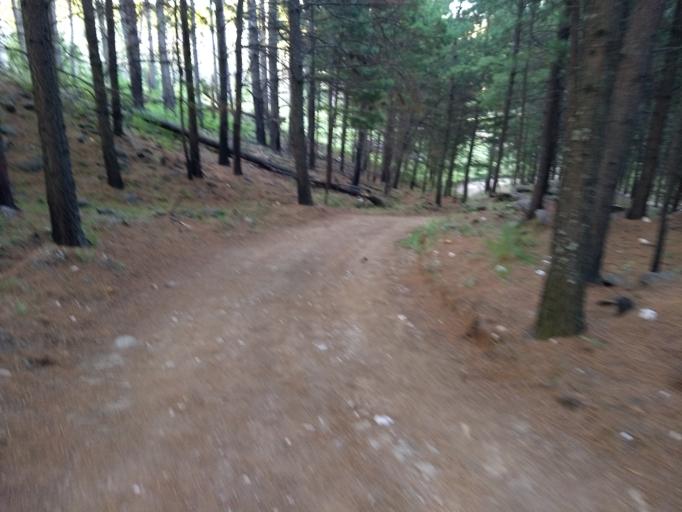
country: AR
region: Cordoba
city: Villa Berna
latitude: -31.9926
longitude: -64.8057
